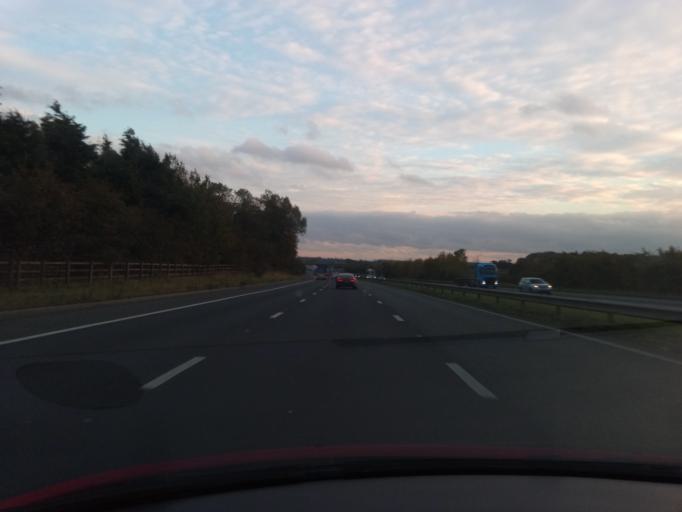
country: GB
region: England
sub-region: City and Borough of Leeds
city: Bramham
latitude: 53.8965
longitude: -1.3694
